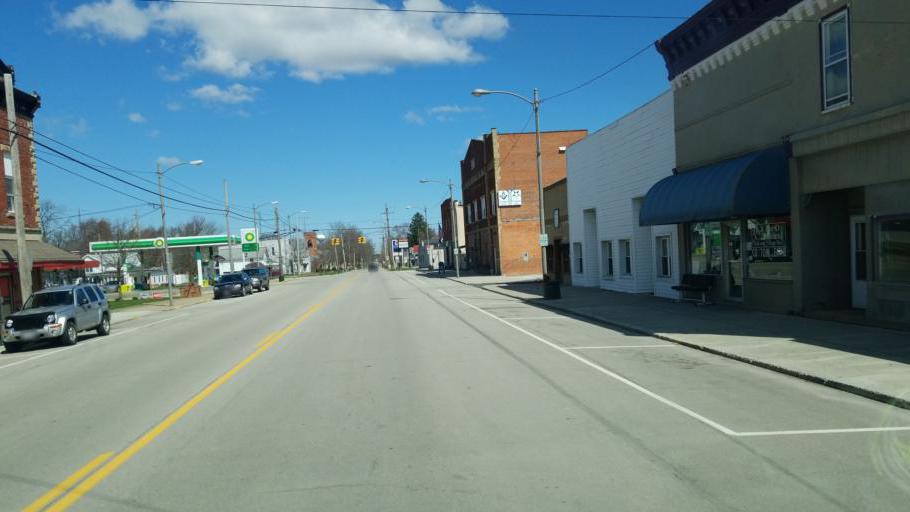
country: US
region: Ohio
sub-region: Sandusky County
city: Green Springs
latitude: 41.2557
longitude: -83.0521
